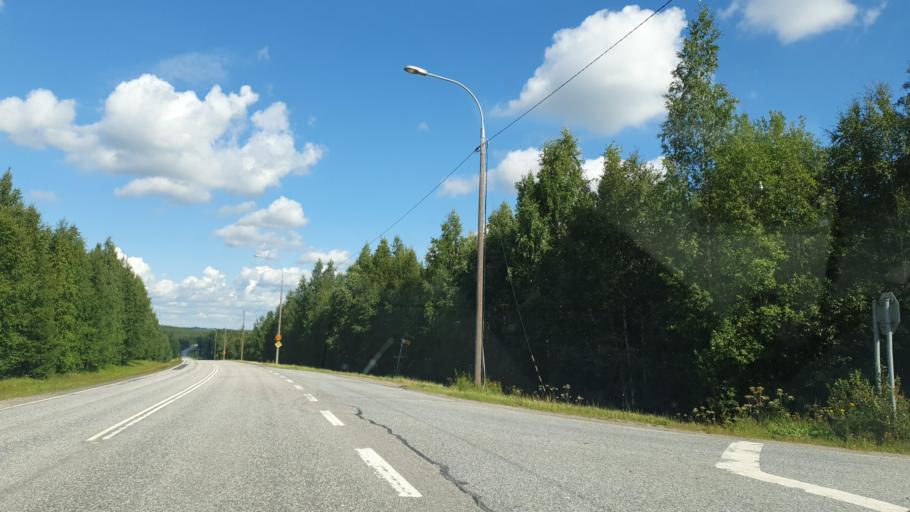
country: FI
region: Northern Savo
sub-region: Ylae-Savo
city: Sonkajaervi
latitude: 63.6978
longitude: 27.3560
